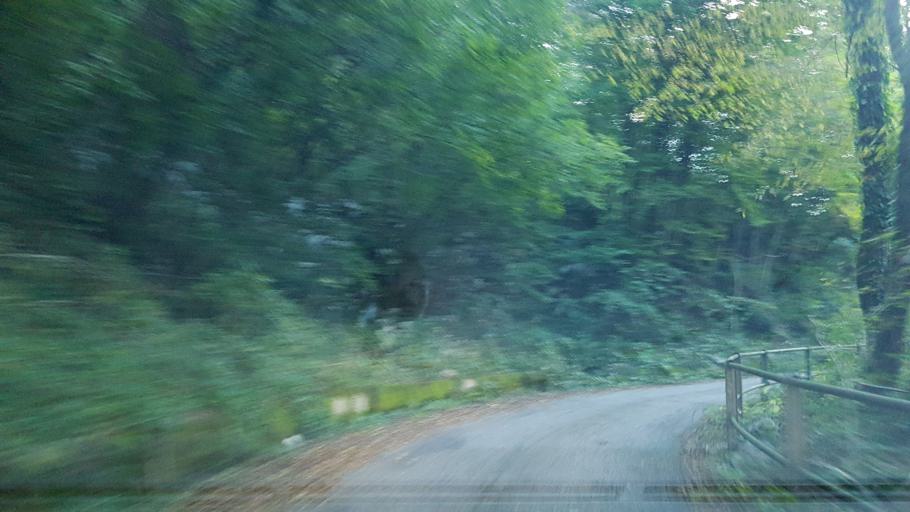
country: IT
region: Friuli Venezia Giulia
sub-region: Provincia di Udine
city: Venzone
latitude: 46.3356
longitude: 13.1714
